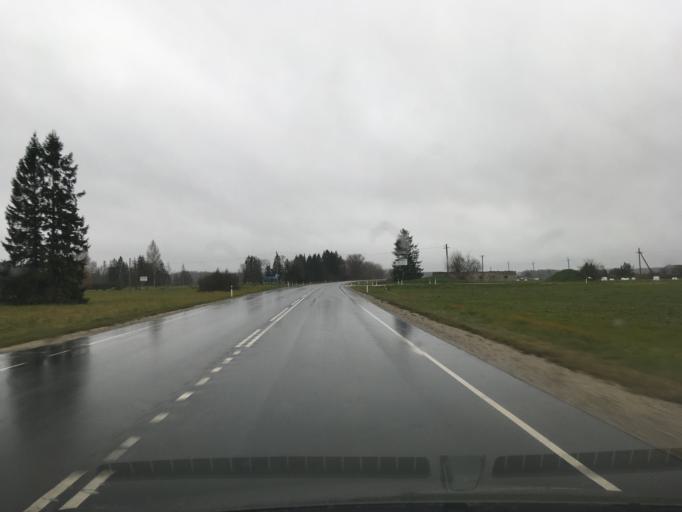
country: EE
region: Harju
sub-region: Nissi vald
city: Turba
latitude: 58.8756
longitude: 24.0863
